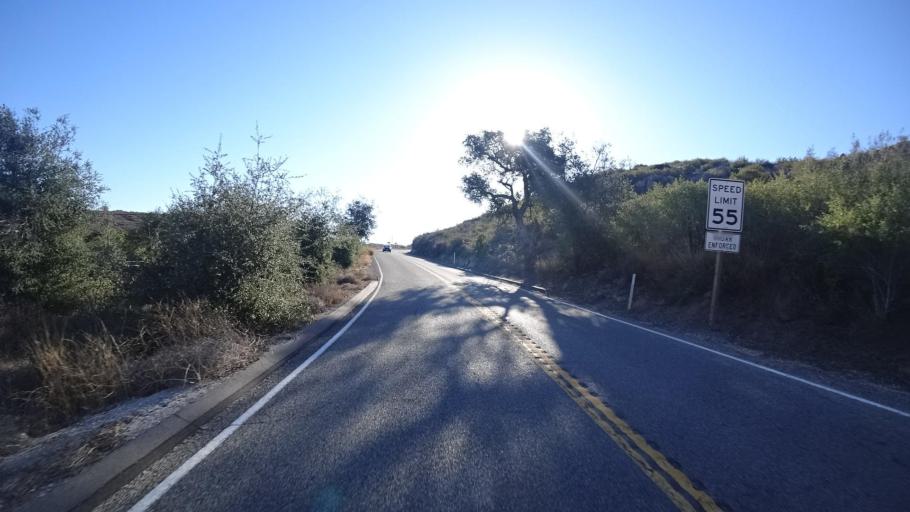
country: MX
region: Baja California
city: Tecate
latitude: 32.6033
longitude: -116.6060
